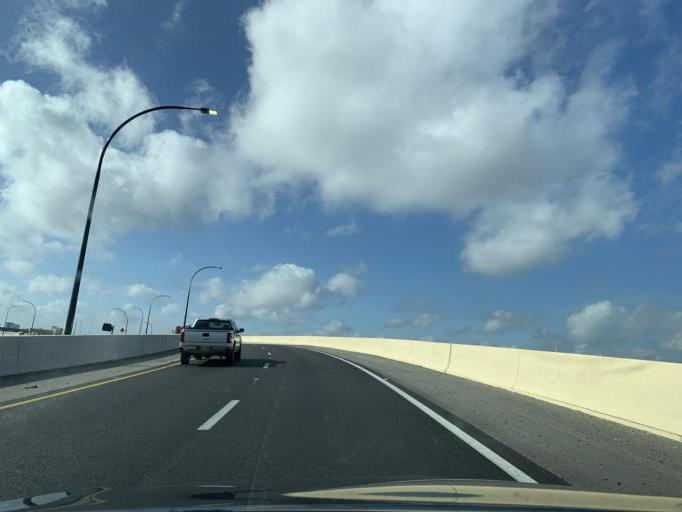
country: US
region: Florida
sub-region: Orange County
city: Tangelo Park
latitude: 28.4733
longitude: -81.4581
